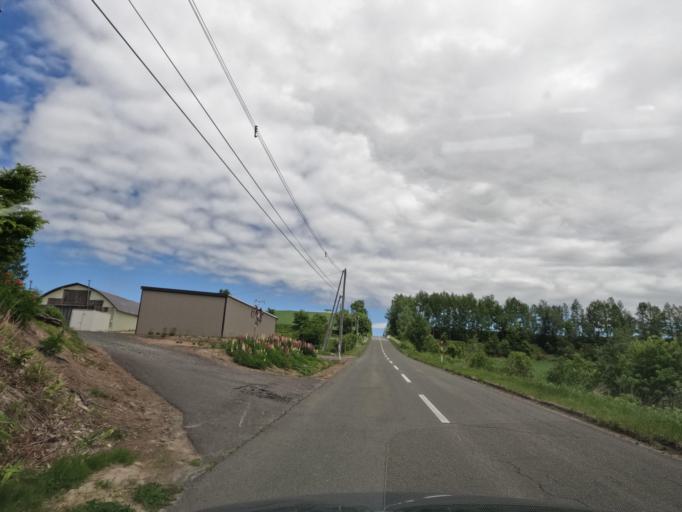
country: JP
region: Hokkaido
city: Shimo-furano
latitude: 43.5183
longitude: 142.4284
